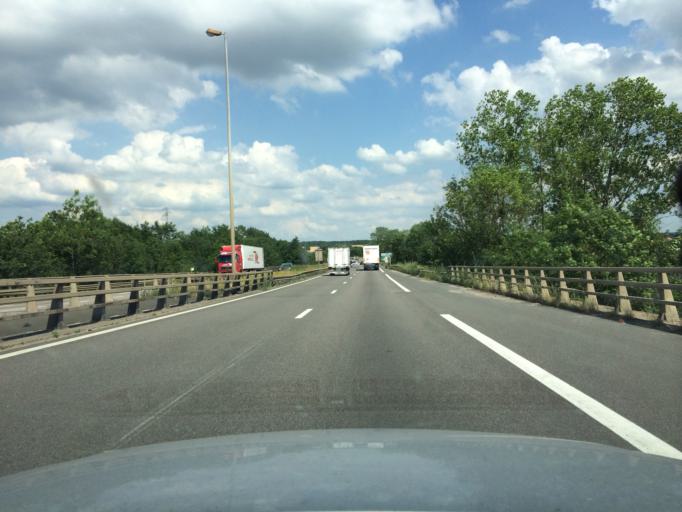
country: FR
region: Lorraine
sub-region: Departement de Meurthe-et-Moselle
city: Dommartin-les-Toul
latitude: 48.6560
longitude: 5.8937
